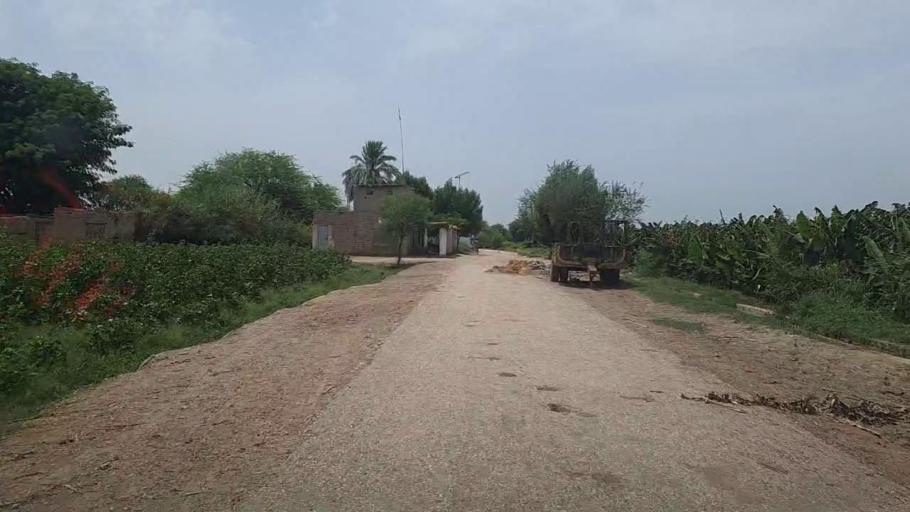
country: PK
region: Sindh
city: Karaundi
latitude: 26.9171
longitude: 68.3333
